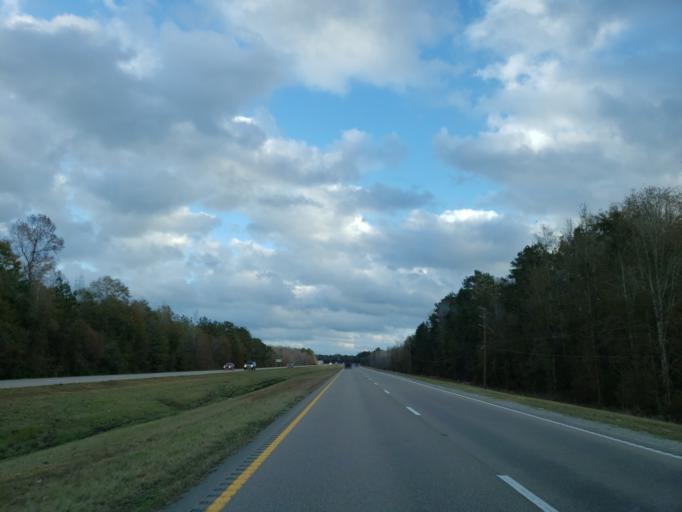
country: US
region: Mississippi
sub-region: Perry County
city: New Augusta
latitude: 31.1500
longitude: -88.8890
